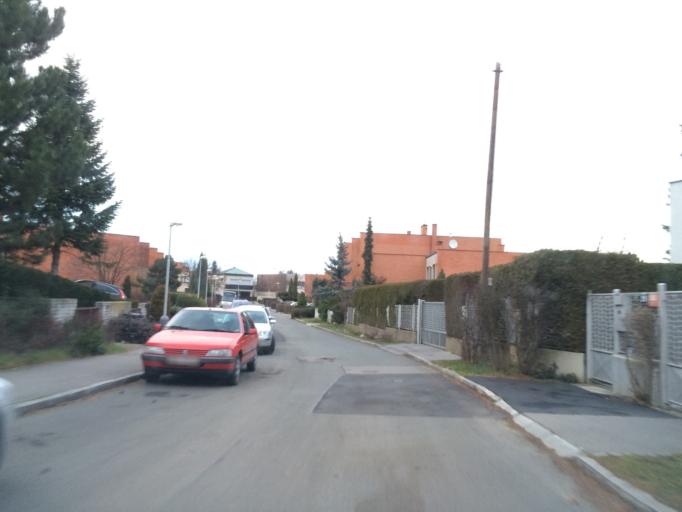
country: CZ
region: Praha
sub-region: Praha 1
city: Mala Strana
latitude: 50.1170
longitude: 14.3886
